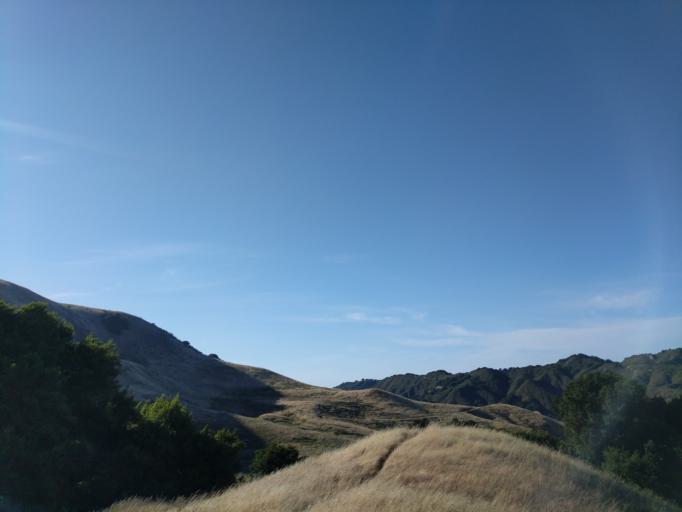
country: US
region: California
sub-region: Contra Costa County
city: Alamo
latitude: 37.8081
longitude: -122.0528
